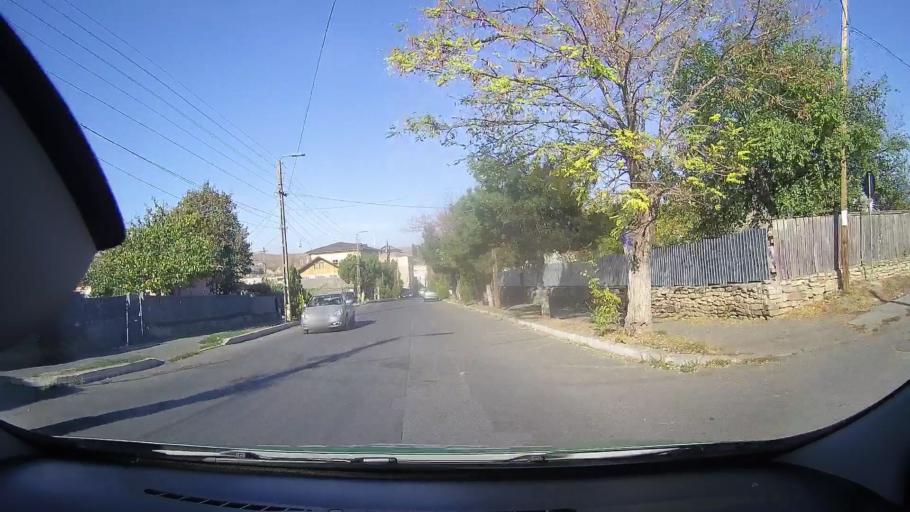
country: RO
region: Tulcea
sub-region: Oras Babadag
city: Babadag
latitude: 44.8919
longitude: 28.7266
